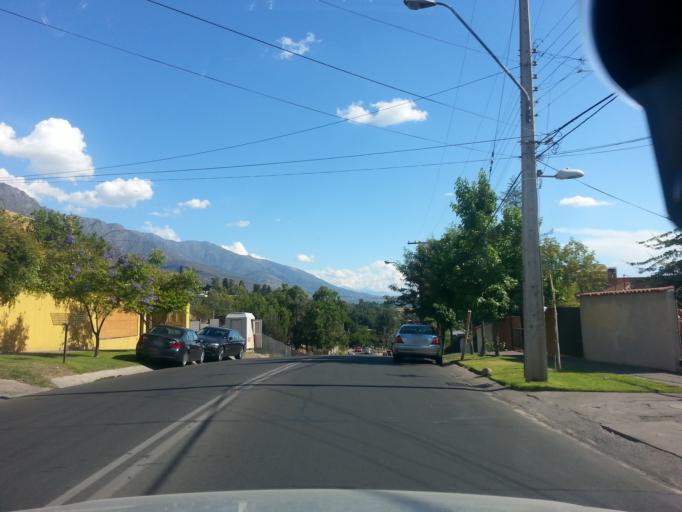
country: CL
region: Santiago Metropolitan
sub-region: Provincia de Santiago
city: Villa Presidente Frei, Nunoa, Santiago, Chile
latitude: -33.4147
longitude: -70.5297
